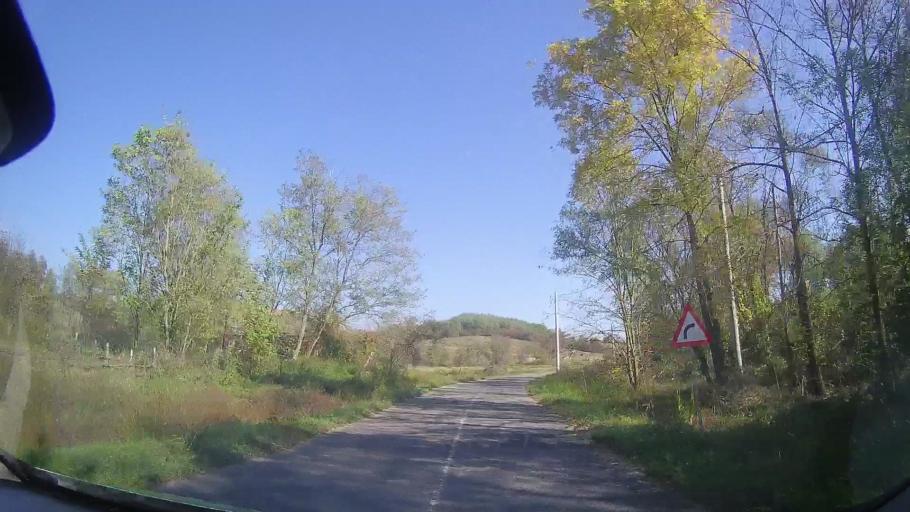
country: RO
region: Timis
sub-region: Comuna Bara
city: Bara
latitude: 45.8966
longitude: 21.9249
